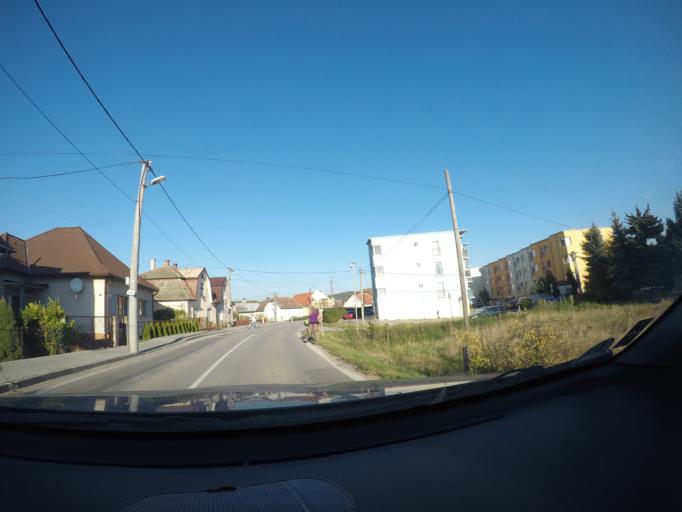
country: SK
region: Trenciansky
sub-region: Okres Trencin
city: Trencin
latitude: 48.9015
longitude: 18.0333
